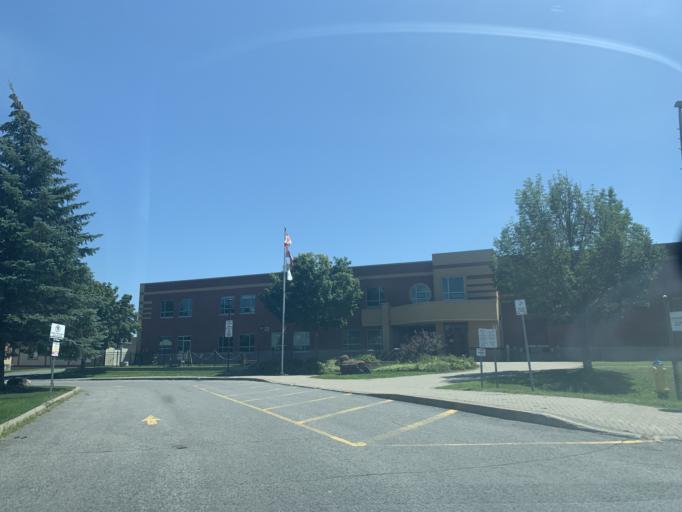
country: CA
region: Ontario
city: Hawkesbury
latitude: 45.6067
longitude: -74.6018
